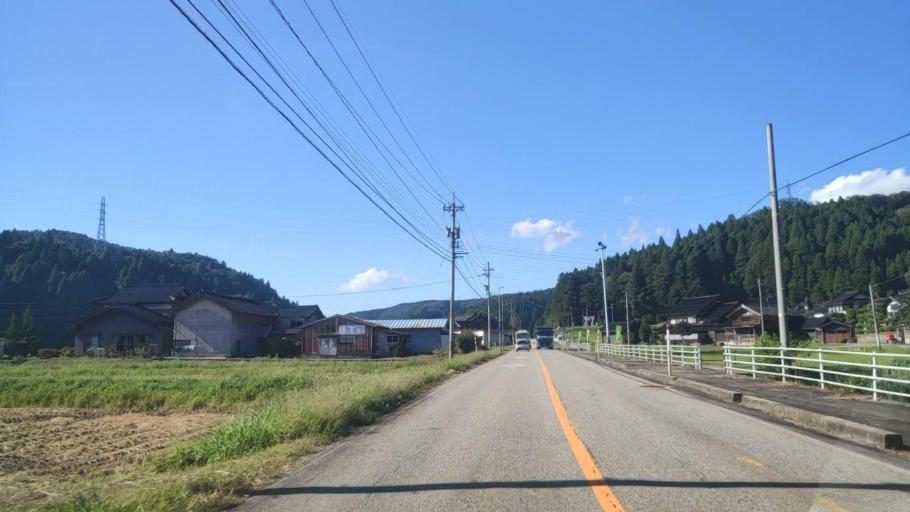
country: JP
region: Ishikawa
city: Nanao
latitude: 37.2717
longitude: 137.0562
